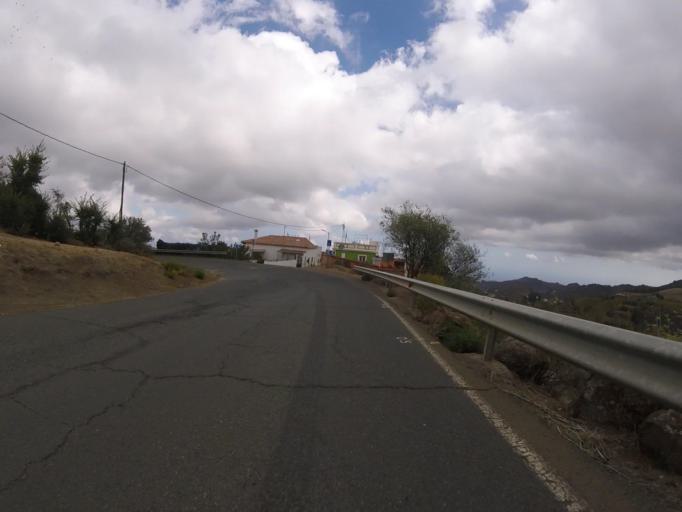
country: ES
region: Canary Islands
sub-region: Provincia de Las Palmas
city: Vega de San Mateo
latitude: 27.9988
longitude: -15.5665
